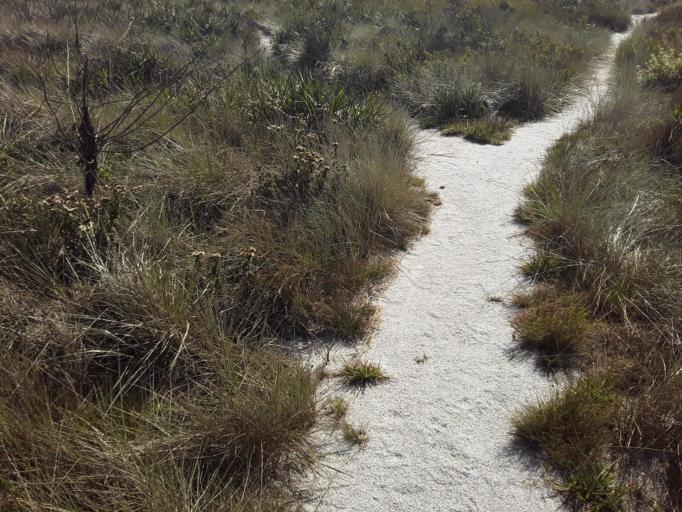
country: BR
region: Minas Gerais
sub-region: Lima Duarte
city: Lima Duarte
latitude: -21.6969
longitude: -43.8979
